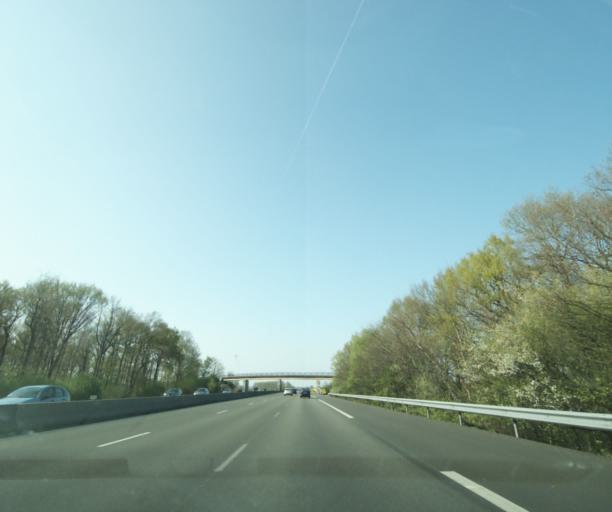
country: FR
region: Ile-de-France
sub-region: Departement de l'Essonne
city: Soisy-sur-Ecole
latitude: 48.5061
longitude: 2.5118
